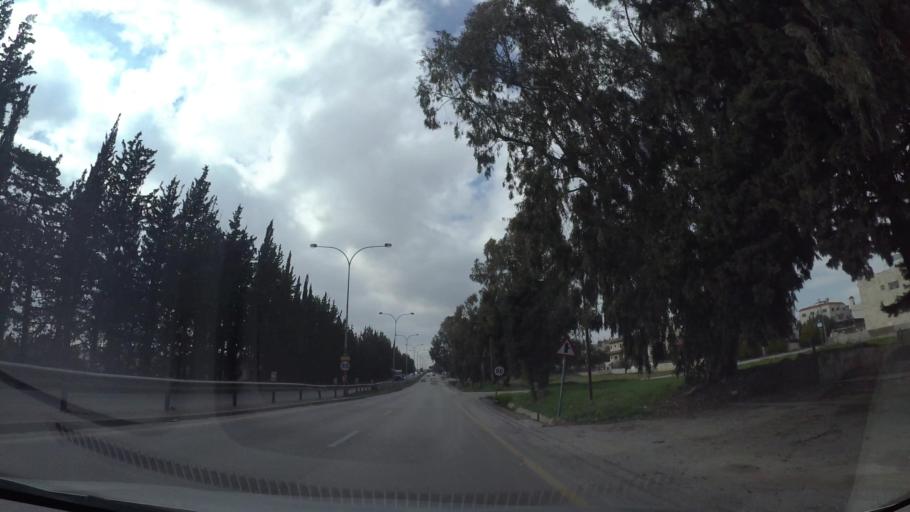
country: JO
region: Amman
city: Al Jubayhah
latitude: 32.0284
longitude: 35.8131
